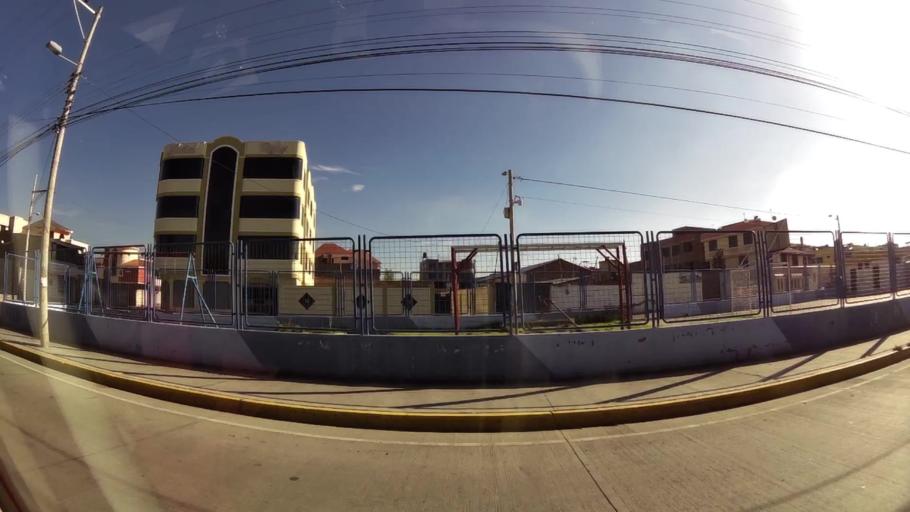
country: EC
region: Chimborazo
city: Riobamba
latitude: -1.6694
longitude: -78.6658
